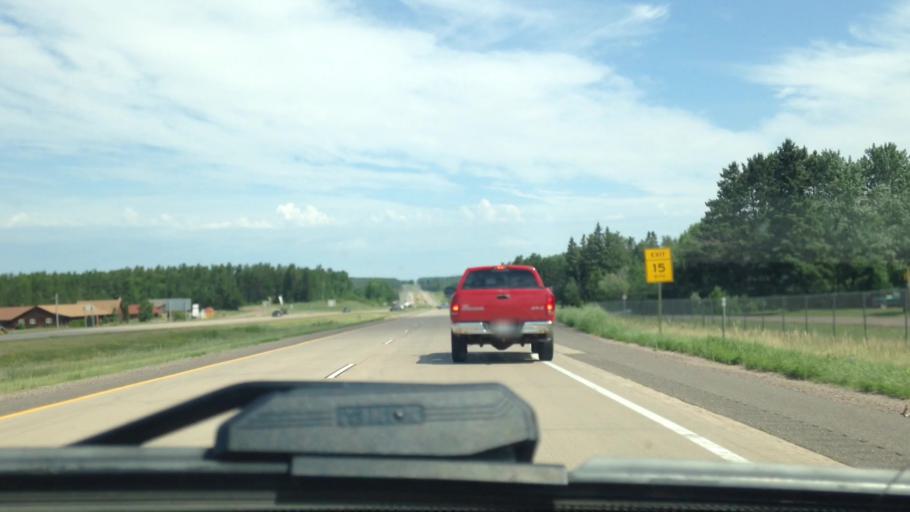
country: US
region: Wisconsin
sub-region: Washburn County
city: Spooner
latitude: 45.9028
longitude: -91.8279
